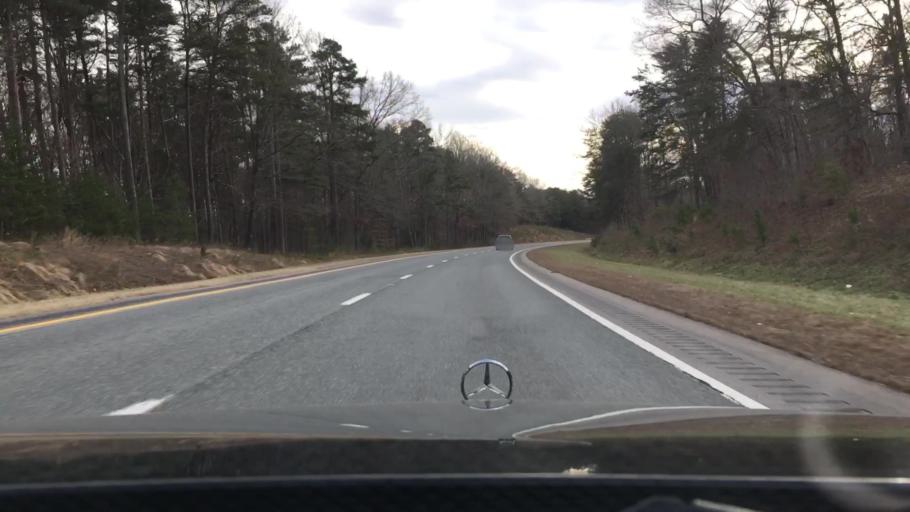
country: US
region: Virginia
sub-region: Pittsylvania County
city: Gretna
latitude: 36.9303
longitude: -79.3761
